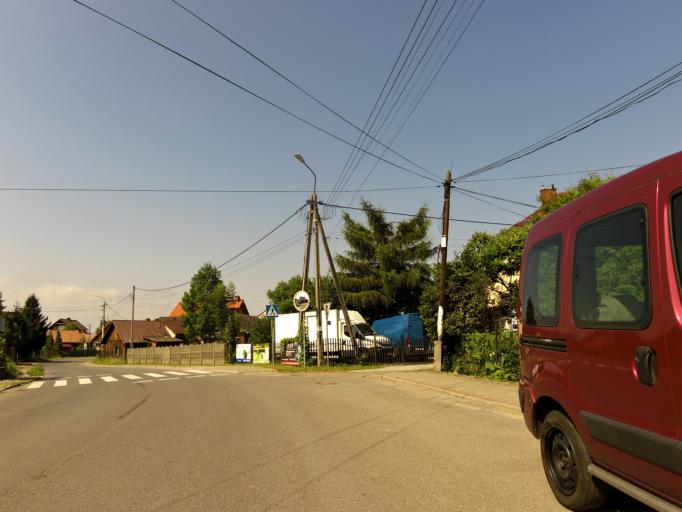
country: PL
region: Silesian Voivodeship
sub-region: Powiat zywiecki
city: Wieprz
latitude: 49.6441
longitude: 19.1786
